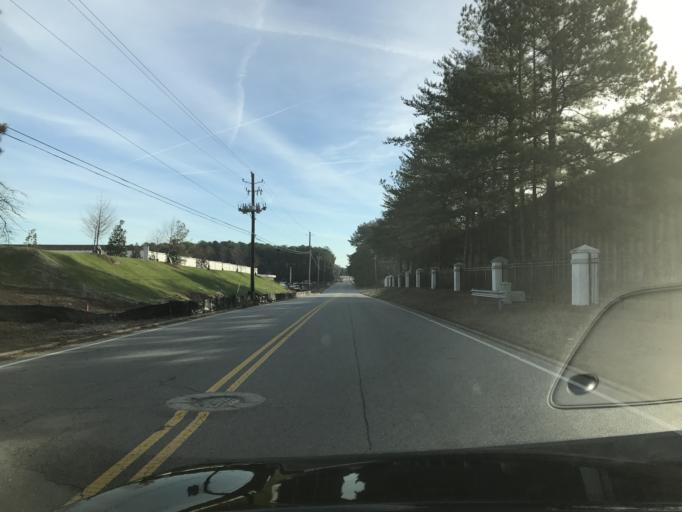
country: US
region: Georgia
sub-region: Clayton County
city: Morrow
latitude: 33.5641
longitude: -84.3529
